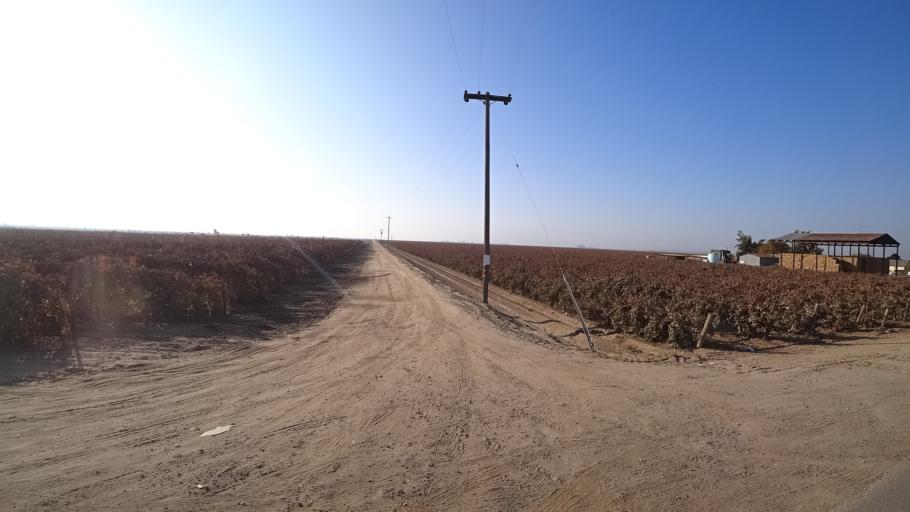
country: US
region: California
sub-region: Kern County
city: Weedpatch
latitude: 35.2378
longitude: -118.9454
